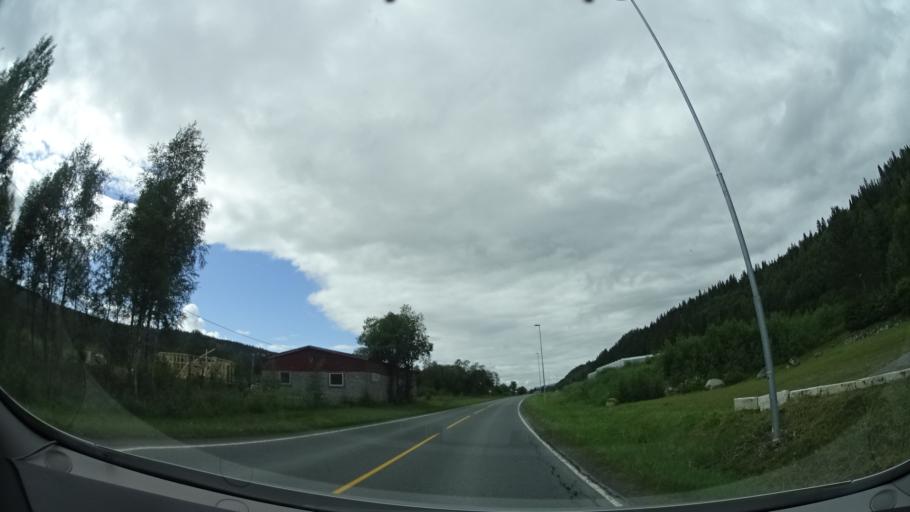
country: NO
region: Nord-Trondelag
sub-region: Meraker
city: Meraker
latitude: 63.3979
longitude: 11.7868
